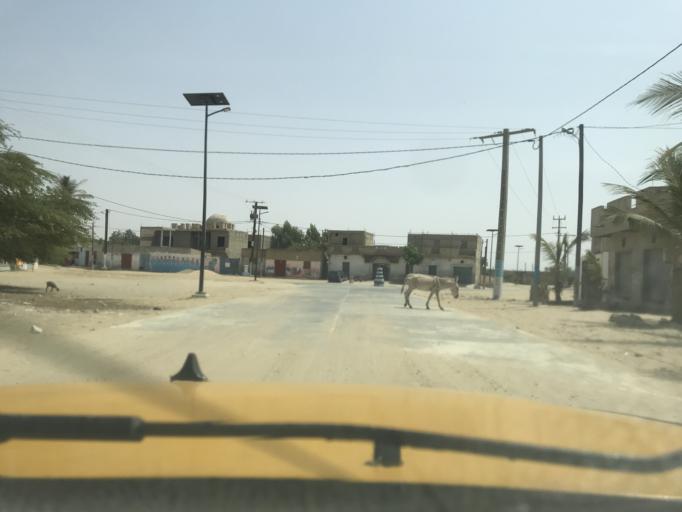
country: SN
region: Saint-Louis
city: Saint-Louis
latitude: 16.0196
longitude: -16.4467
